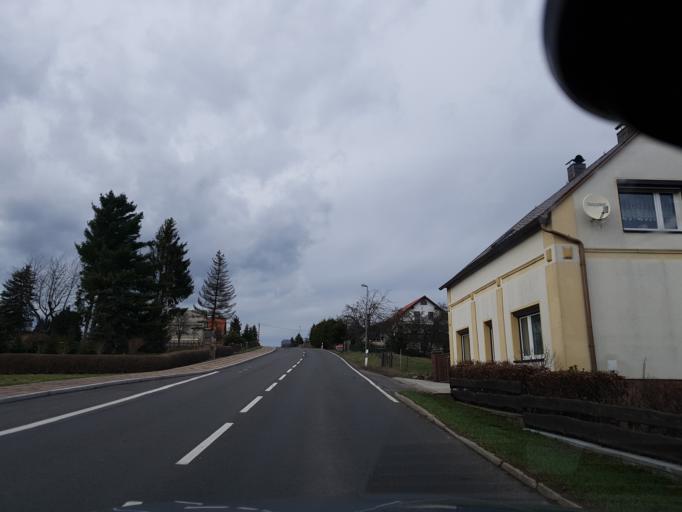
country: DE
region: Saxony
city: Hainichen
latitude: 51.0101
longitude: 13.1299
